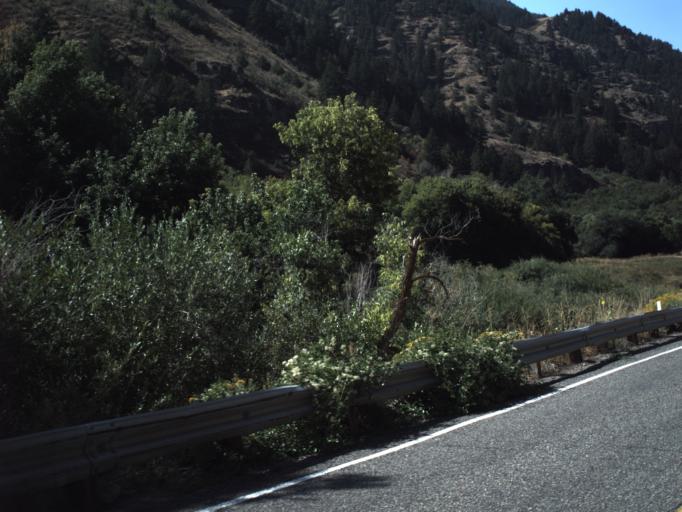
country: US
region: Utah
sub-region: Cache County
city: Millville
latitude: 41.6214
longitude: -111.7506
